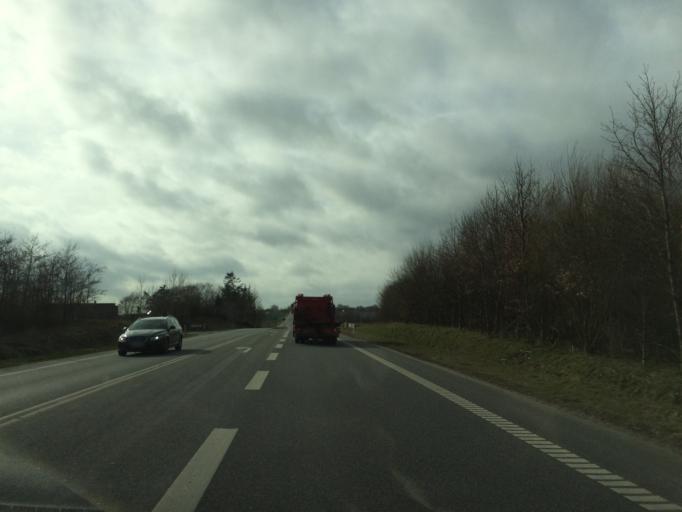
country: DK
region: Central Jutland
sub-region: Randers Kommune
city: Langa
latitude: 56.4774
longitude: 9.9132
